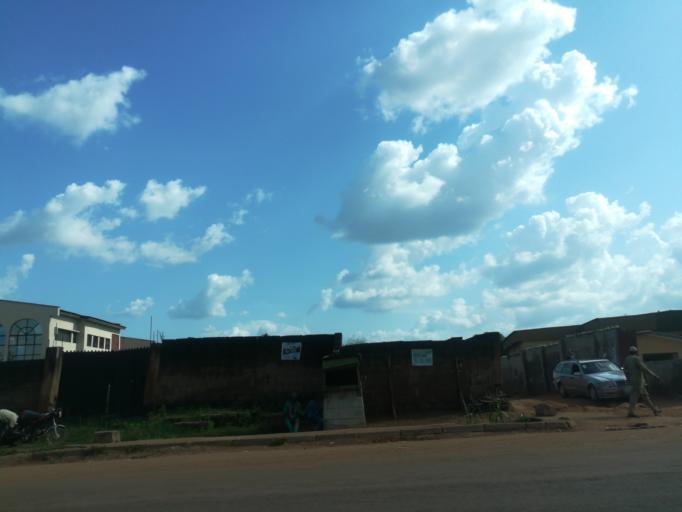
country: NG
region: Oyo
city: Egbeda
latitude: 7.4225
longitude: 3.9781
